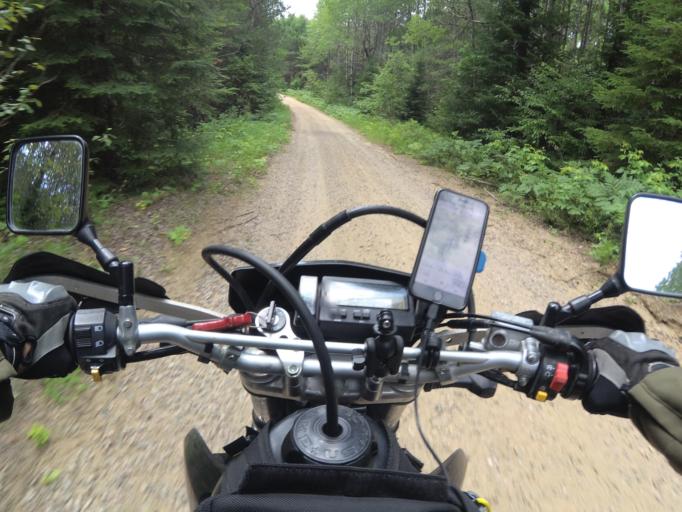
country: CA
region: Ontario
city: Bancroft
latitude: 45.0374
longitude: -77.2611
